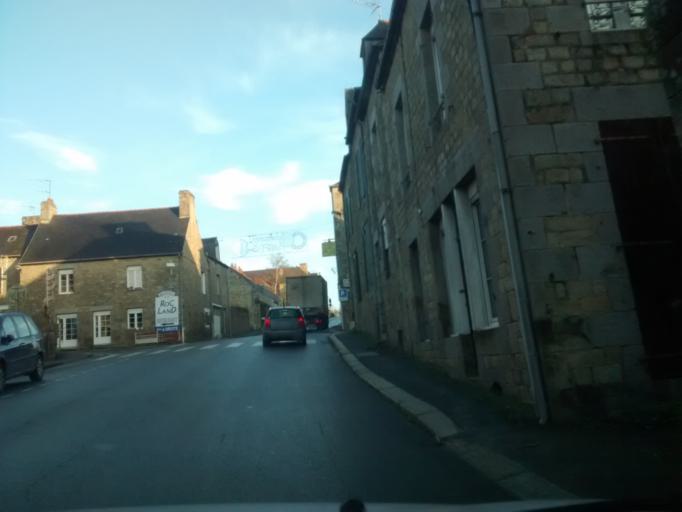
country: FR
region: Brittany
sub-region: Departement d'Ille-et-Vilaine
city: Tremblay
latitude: 48.4221
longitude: -1.4738
